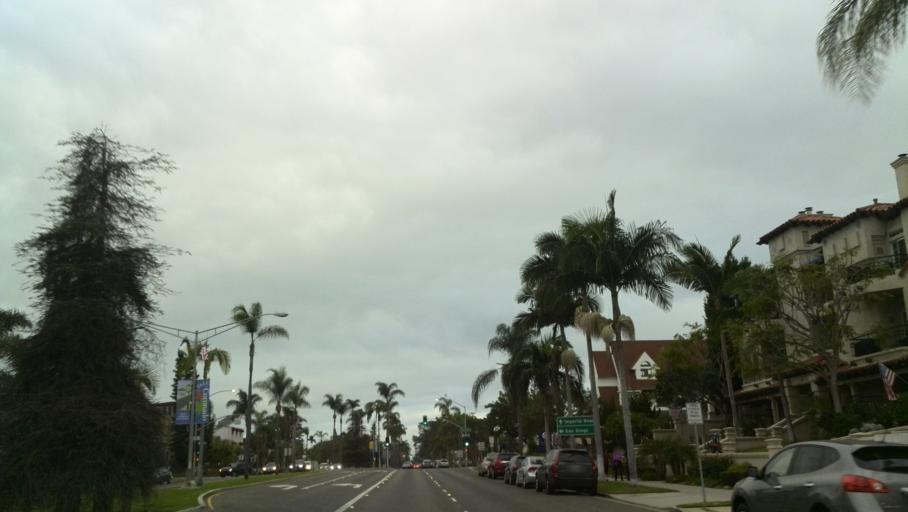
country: US
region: California
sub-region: San Diego County
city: Coronado
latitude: 32.6954
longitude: -117.1744
